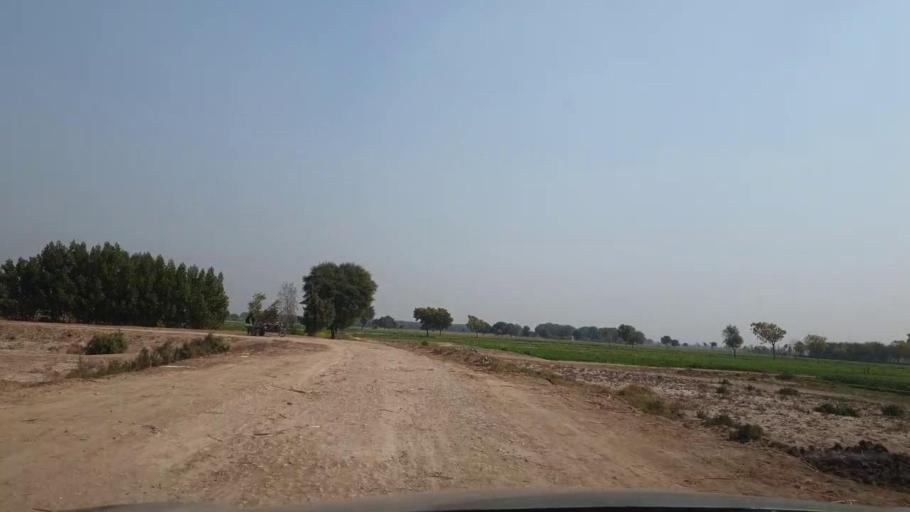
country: PK
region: Sindh
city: Tando Allahyar
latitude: 25.5485
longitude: 68.7136
